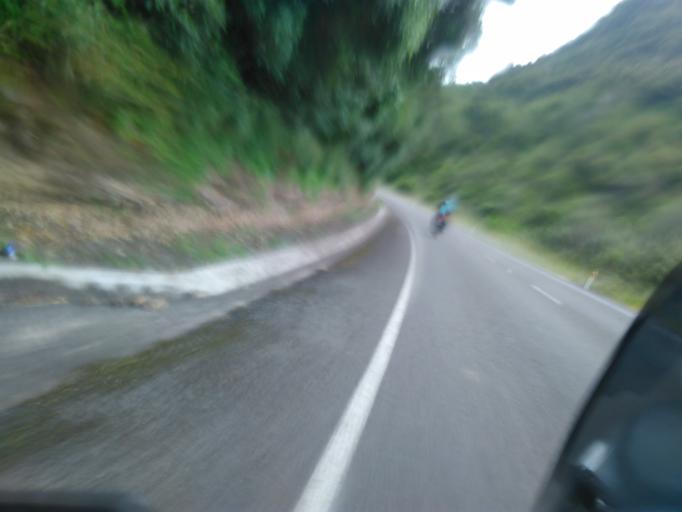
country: NZ
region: Bay of Plenty
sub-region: Opotiki District
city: Opotiki
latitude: -38.3191
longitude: 177.3957
